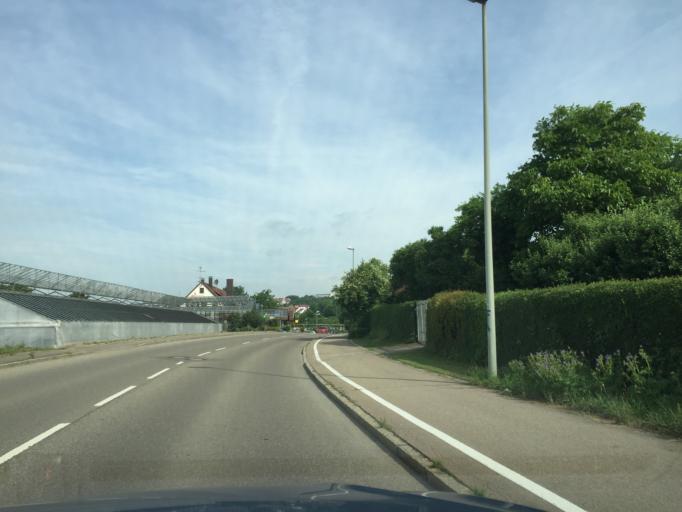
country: DE
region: Baden-Wuerttemberg
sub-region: Tuebingen Region
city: Ulm
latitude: 48.4046
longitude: 9.9515
